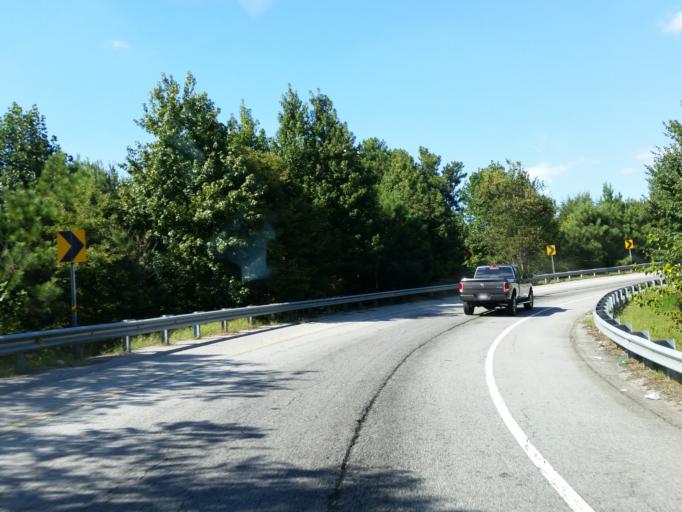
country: US
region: Georgia
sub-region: Fulton County
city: Hapeville
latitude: 33.6315
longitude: -84.4028
